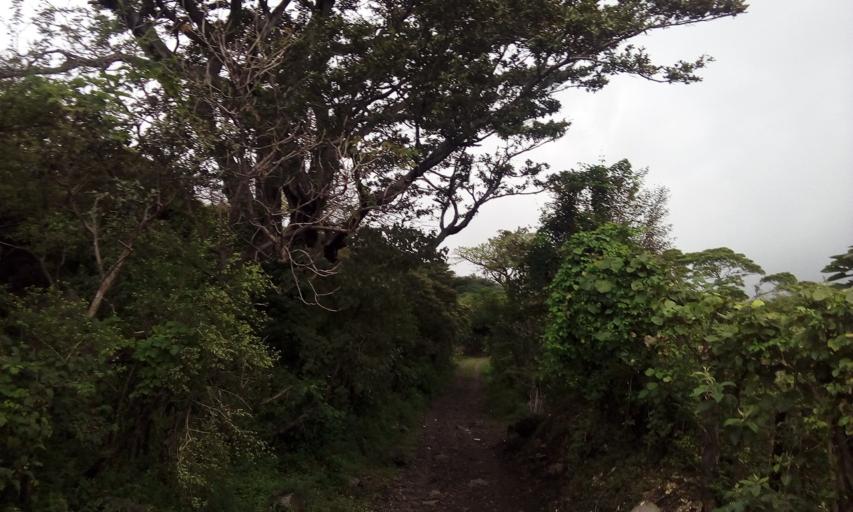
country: GT
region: Escuintla
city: San Vicente Pacaya
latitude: 14.3370
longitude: -90.6126
